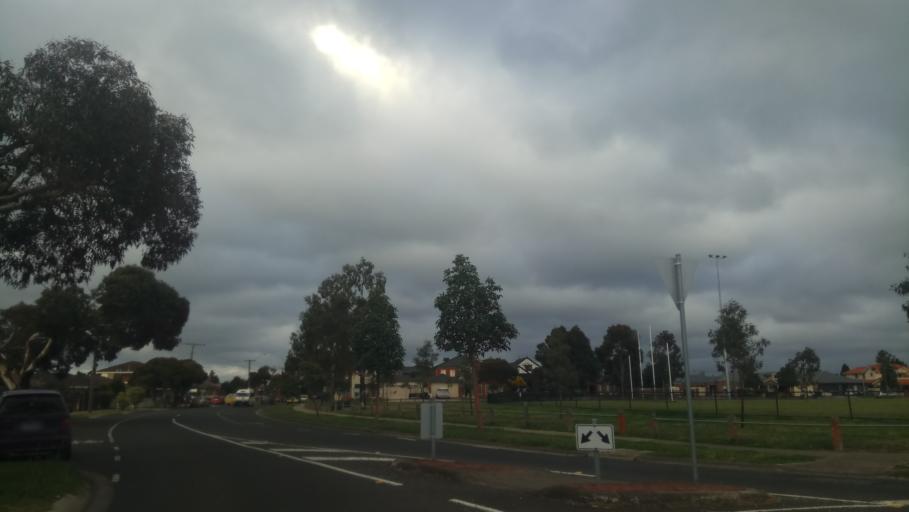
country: AU
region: Victoria
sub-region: Hobsons Bay
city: Altona Meadows
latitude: -37.8884
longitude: 144.7831
